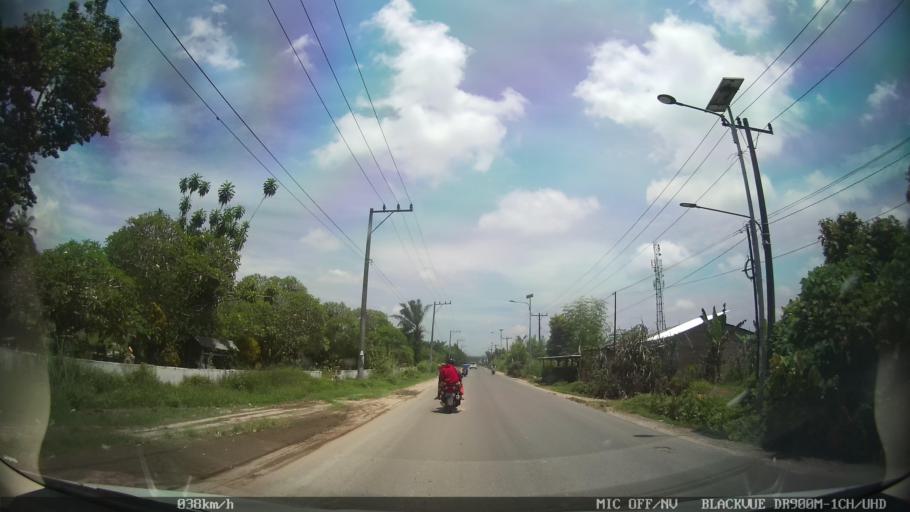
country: ID
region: North Sumatra
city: Perbaungan
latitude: 3.5271
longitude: 98.8883
